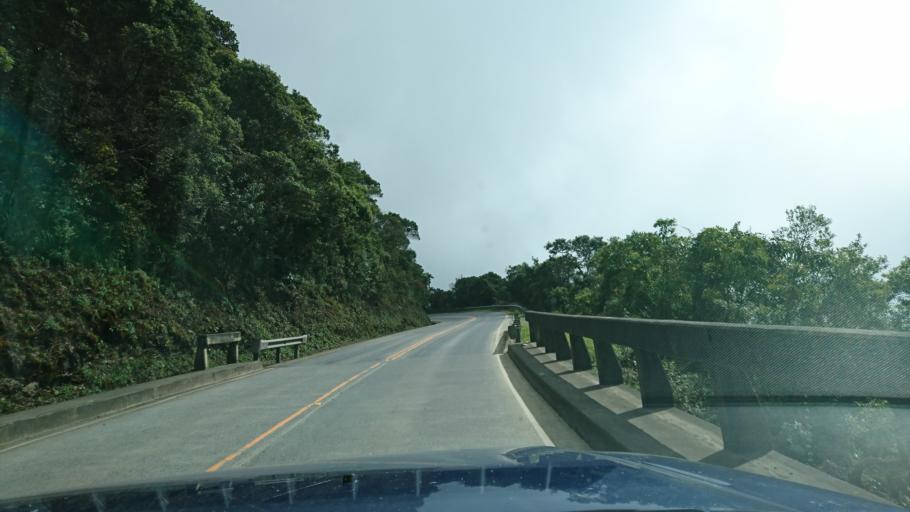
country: BO
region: La Paz
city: Coroico
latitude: -16.2271
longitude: -67.8343
